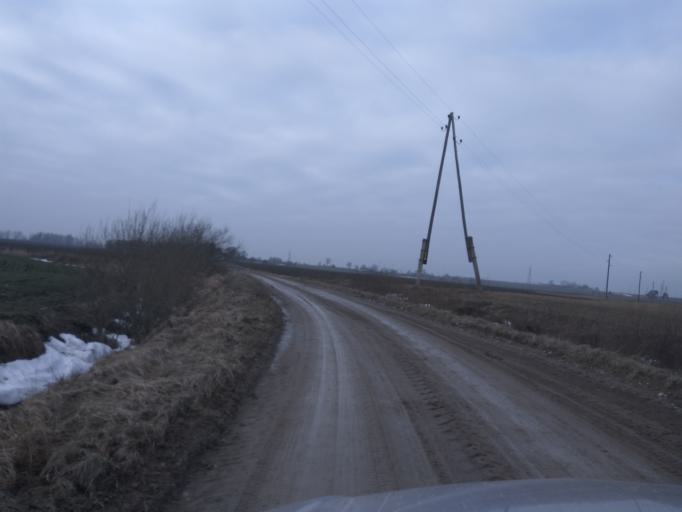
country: LV
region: Durbe
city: Liegi
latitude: 56.6695
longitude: 21.3735
